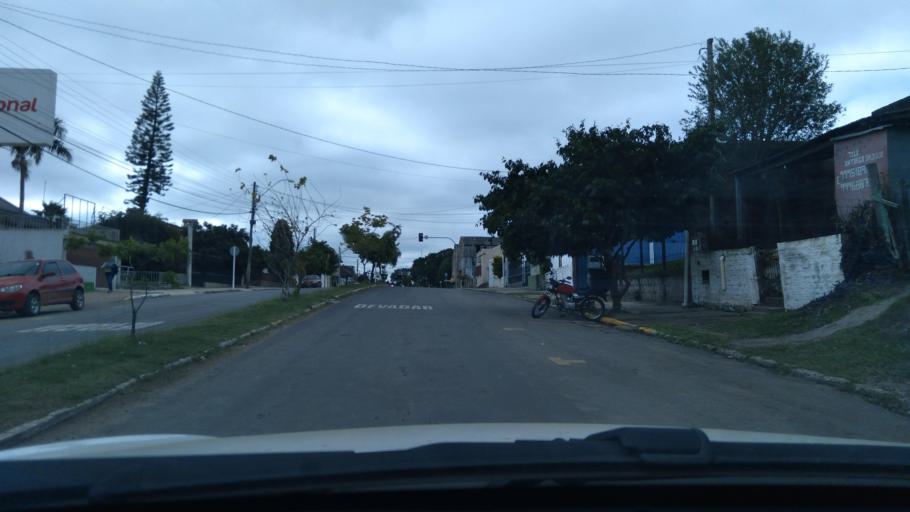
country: BR
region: Rio Grande do Sul
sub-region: Dom Pedrito
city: Dom Pedrito
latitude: -30.9751
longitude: -54.6743
